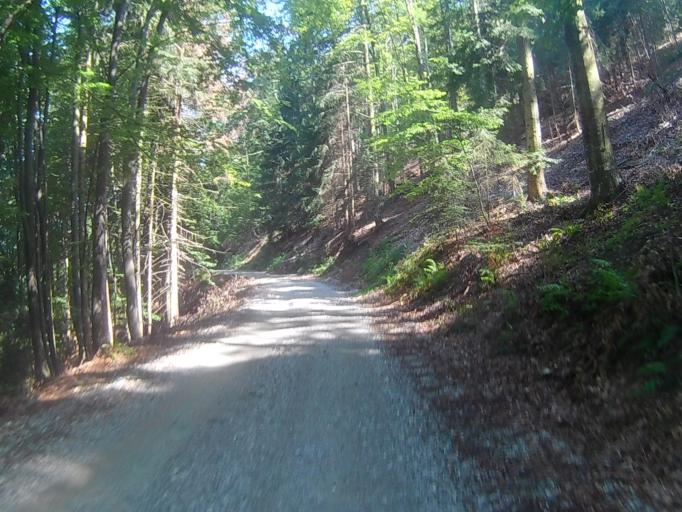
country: SI
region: Ruse
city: Bistrica ob Dravi
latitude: 46.5195
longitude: 15.5552
